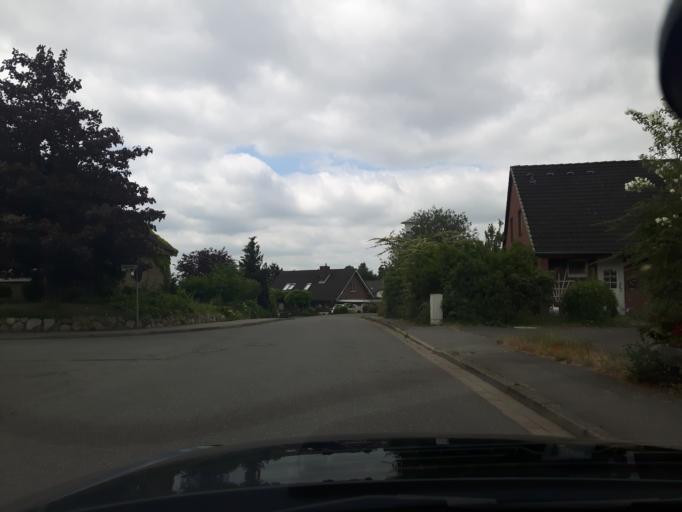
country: DE
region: Schleswig-Holstein
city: Neustadt in Holstein
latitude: 54.0942
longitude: 10.8543
